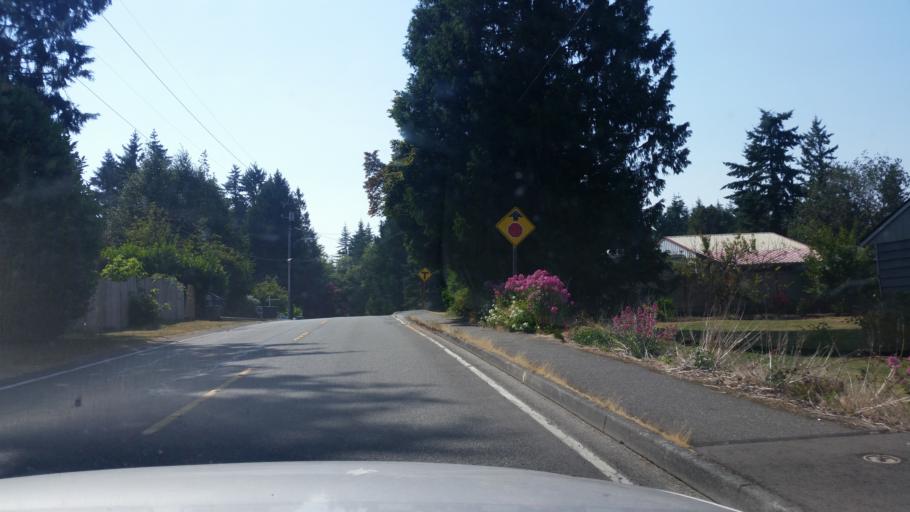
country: US
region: Washington
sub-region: Snohomish County
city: Esperance
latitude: 47.8123
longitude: -122.3424
